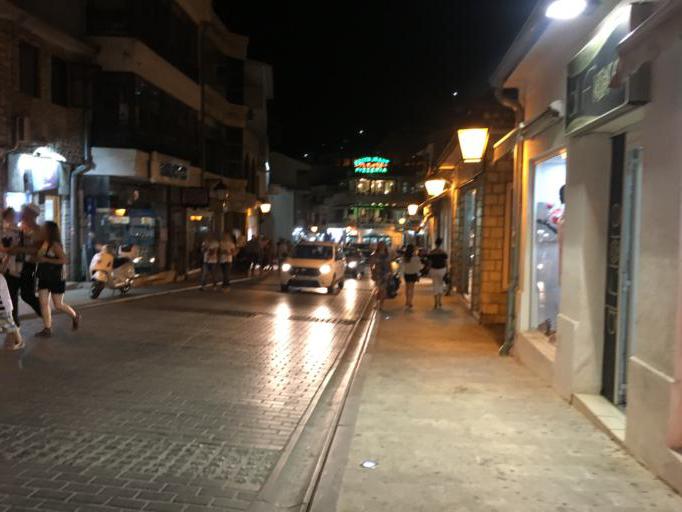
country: ME
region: Ulcinj
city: Ulcinj
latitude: 41.9304
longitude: 19.2081
